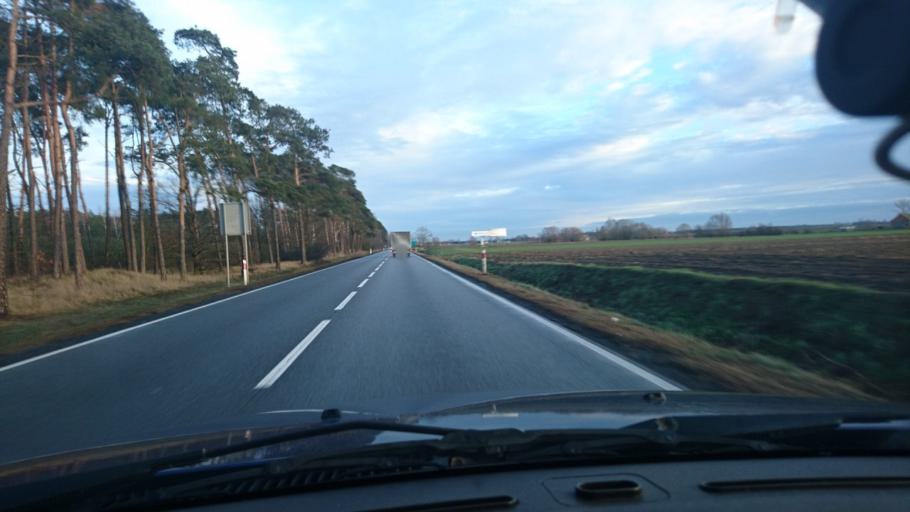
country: PL
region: Greater Poland Voivodeship
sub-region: Powiat kepinski
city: Leka Opatowska
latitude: 51.2226
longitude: 18.1215
